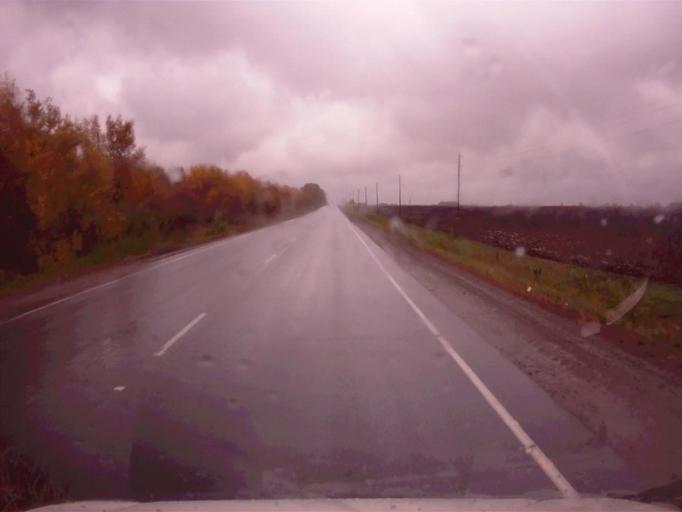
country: RU
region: Chelyabinsk
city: Argayash
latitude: 55.4271
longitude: 60.9996
